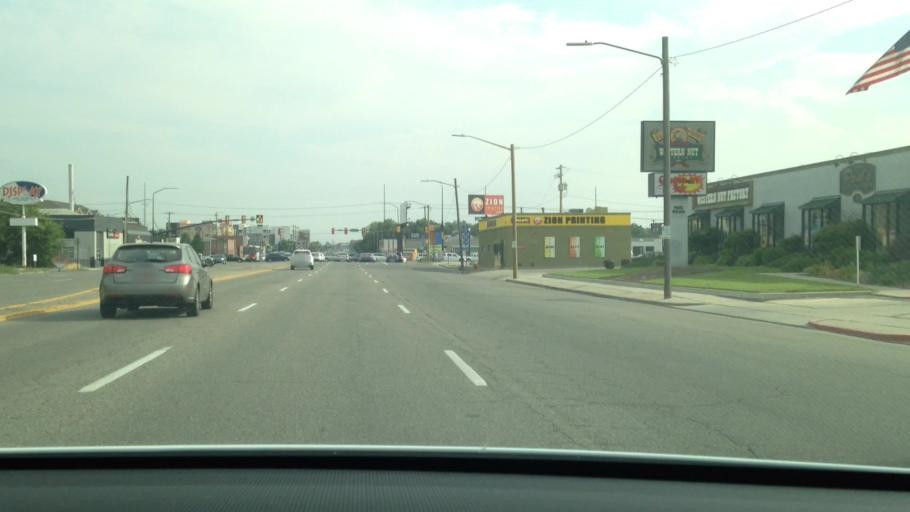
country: US
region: Utah
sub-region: Salt Lake County
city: Salt Lake City
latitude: 40.7601
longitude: -111.8998
